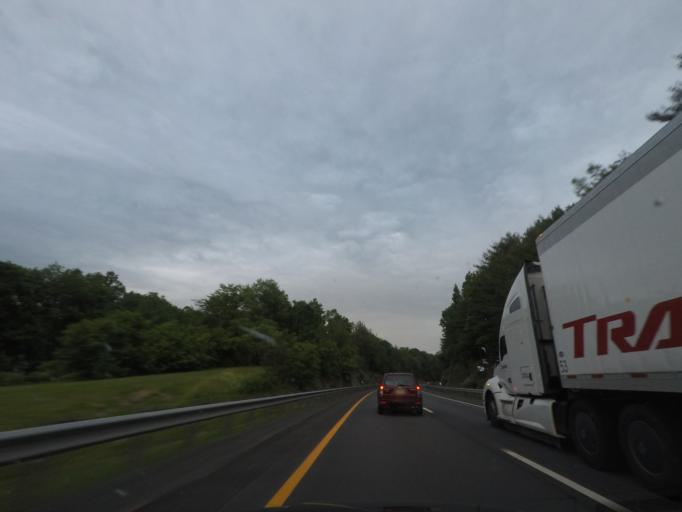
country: US
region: New York
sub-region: Rensselaer County
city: Nassau
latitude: 42.4476
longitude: -73.5695
